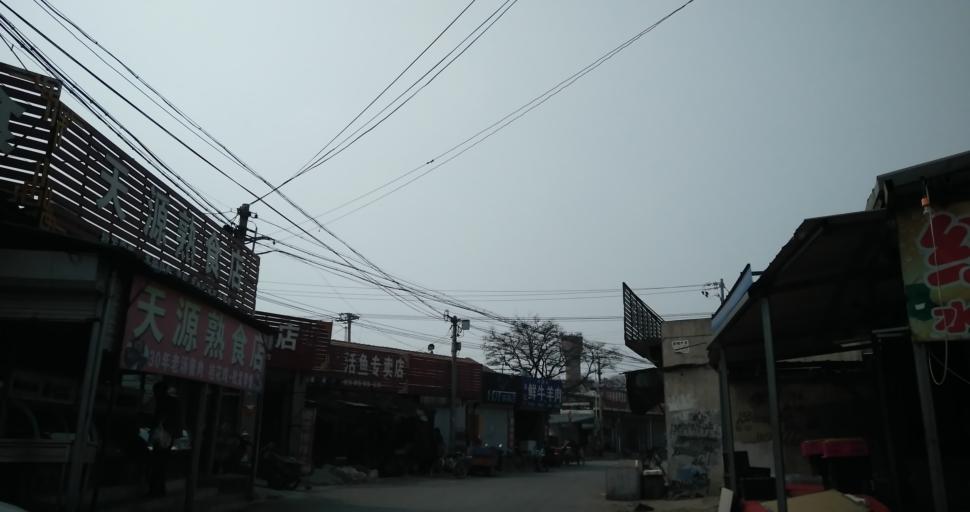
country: CN
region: Beijing
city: Qingyundian
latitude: 39.6785
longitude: 116.5098
